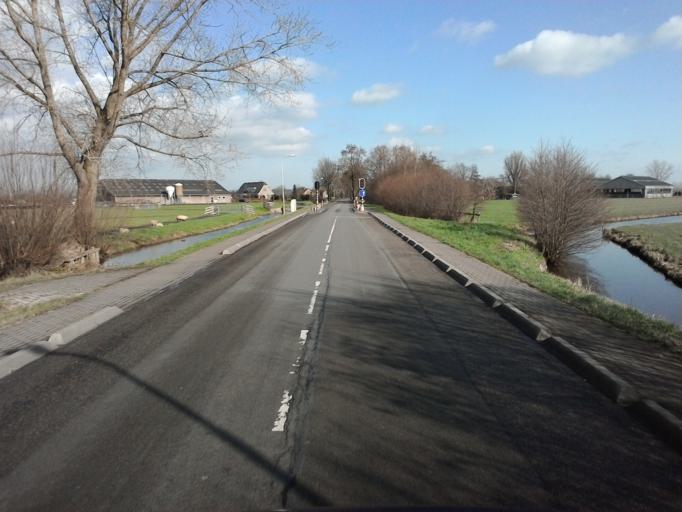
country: NL
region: Utrecht
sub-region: Gemeente Lopik
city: Lopik
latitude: 51.9230
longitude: 5.0083
